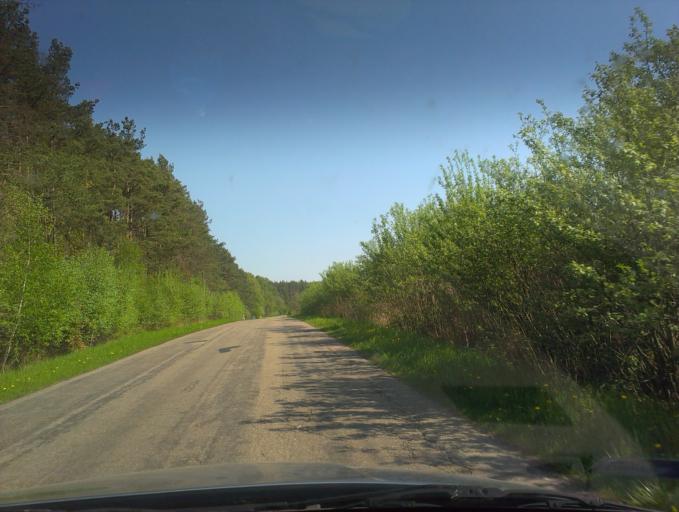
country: PL
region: West Pomeranian Voivodeship
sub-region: Powiat szczecinecki
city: Barwice
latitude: 53.6867
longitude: 16.3430
